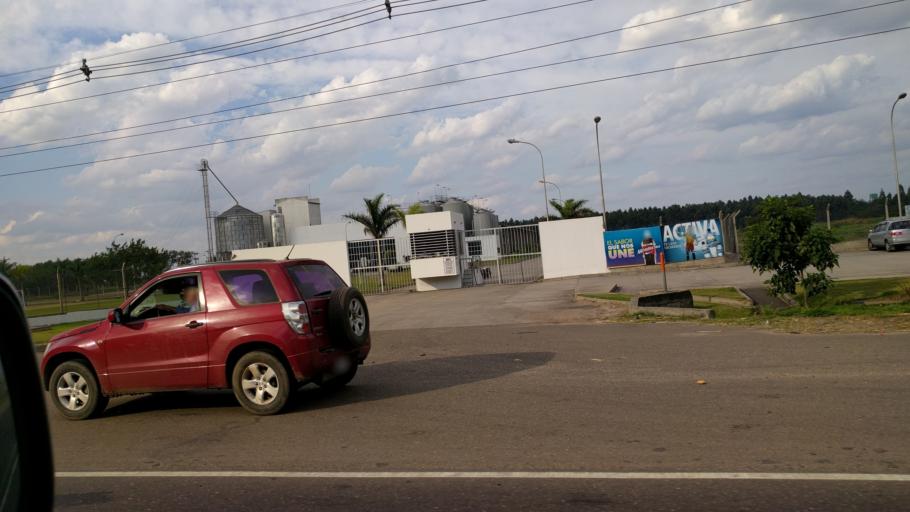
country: BO
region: Santa Cruz
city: La Belgica
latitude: -17.5598
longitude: -63.1593
